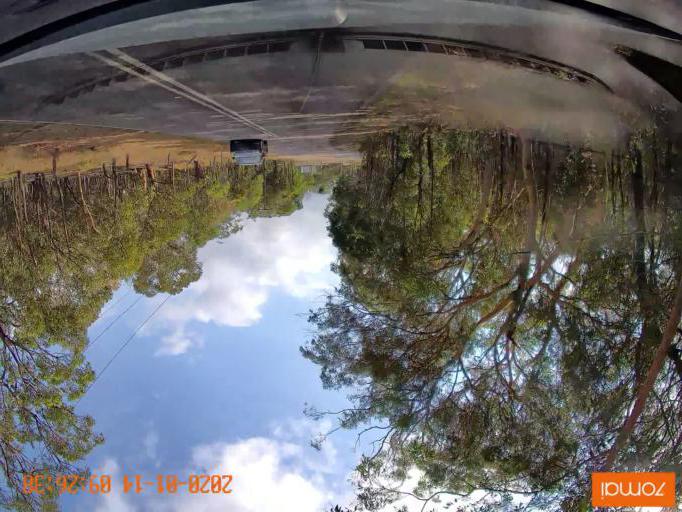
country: AU
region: New South Wales
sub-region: Lake Macquarie Shire
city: Dora Creek
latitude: -33.1163
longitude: 151.5171
